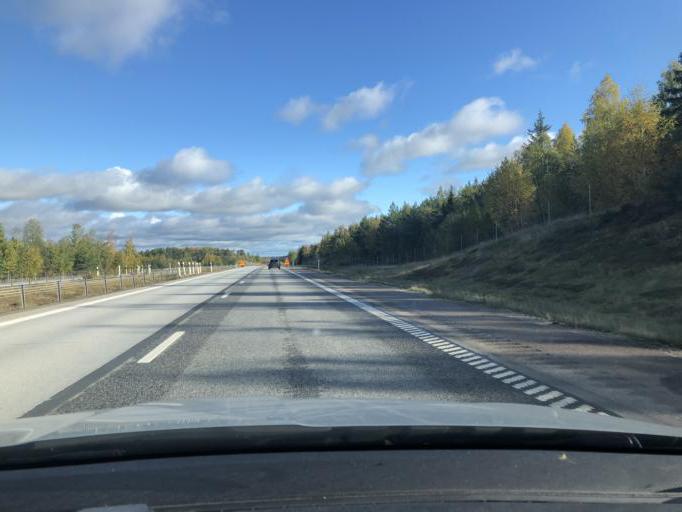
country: SE
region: Soedermanland
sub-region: Eskilstuna Kommun
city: Arla
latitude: 59.3767
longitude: 16.7543
